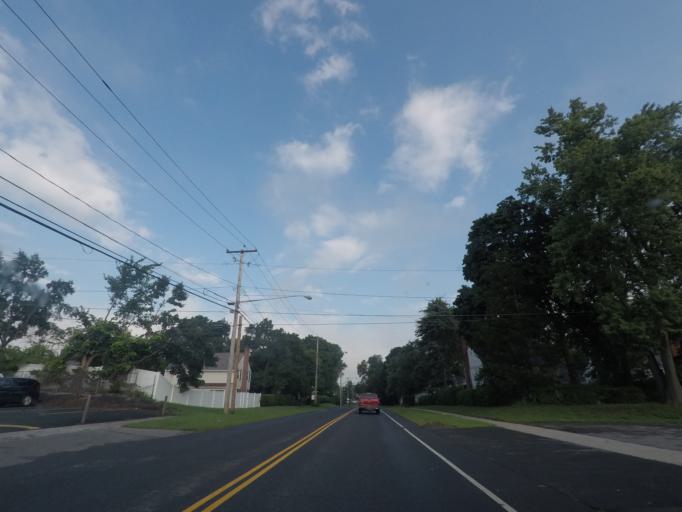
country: US
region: New York
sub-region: Albany County
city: West Albany
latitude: 42.6786
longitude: -73.7966
